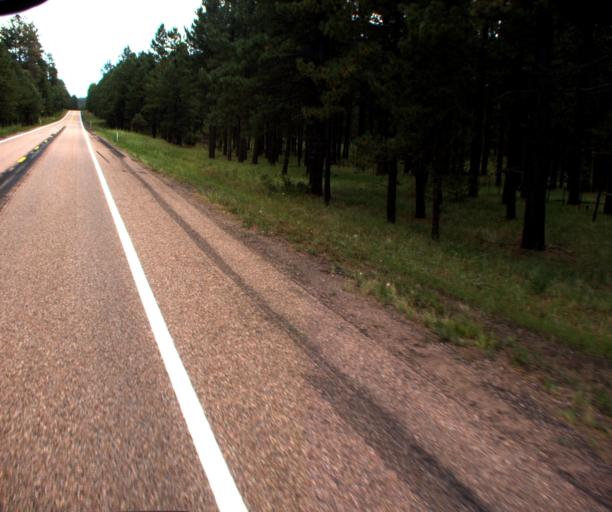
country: US
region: Arizona
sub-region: Navajo County
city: Pinetop-Lakeside
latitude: 34.0404
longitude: -109.6736
